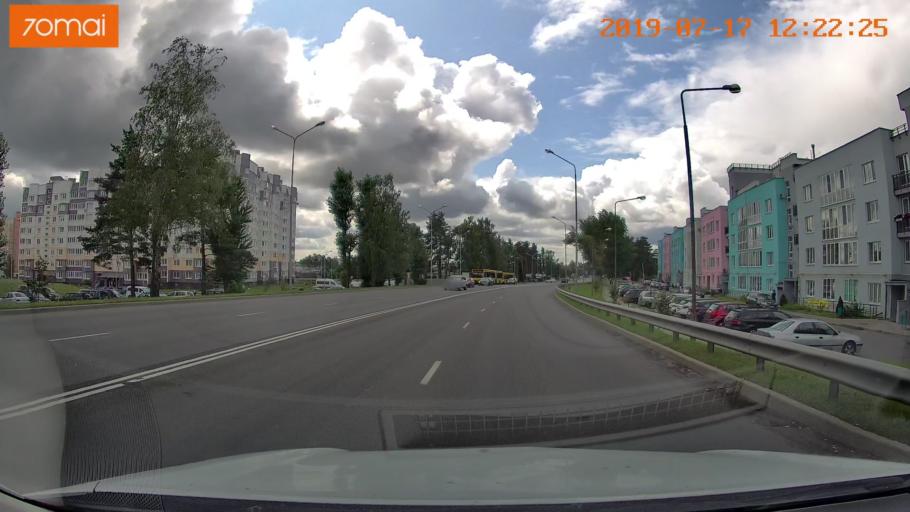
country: BY
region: Minsk
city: Borovlyany
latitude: 54.0016
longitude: 27.6777
